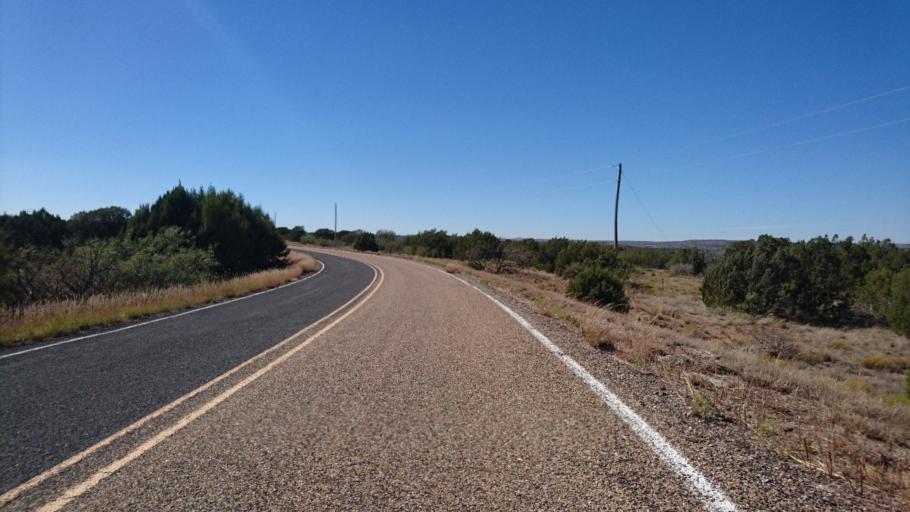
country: US
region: New Mexico
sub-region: Quay County
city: Tucumcari
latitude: 35.0675
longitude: -104.1810
